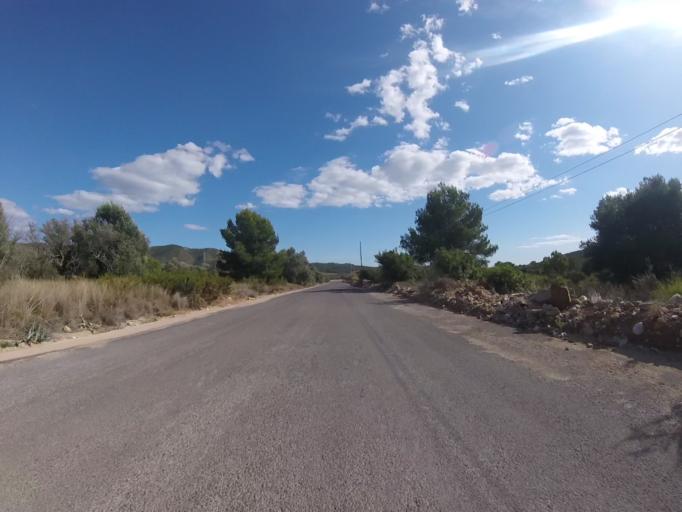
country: ES
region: Valencia
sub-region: Provincia de Castello
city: Alcala de Xivert
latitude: 40.2709
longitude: 0.2388
